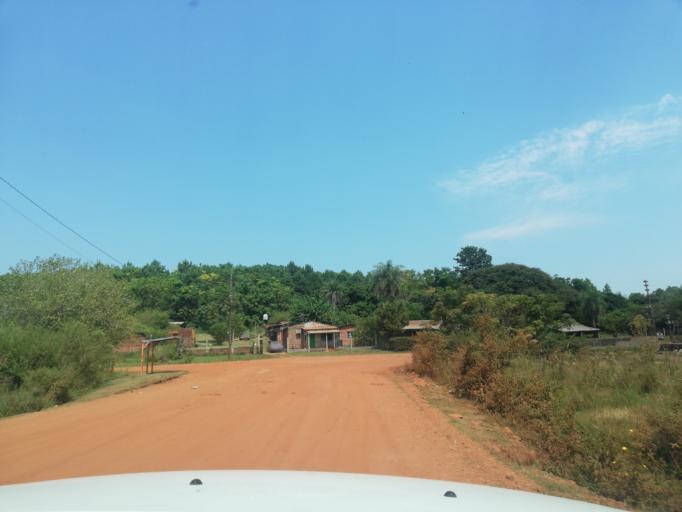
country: AR
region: Misiones
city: Garupa
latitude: -27.4504
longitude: -55.8947
